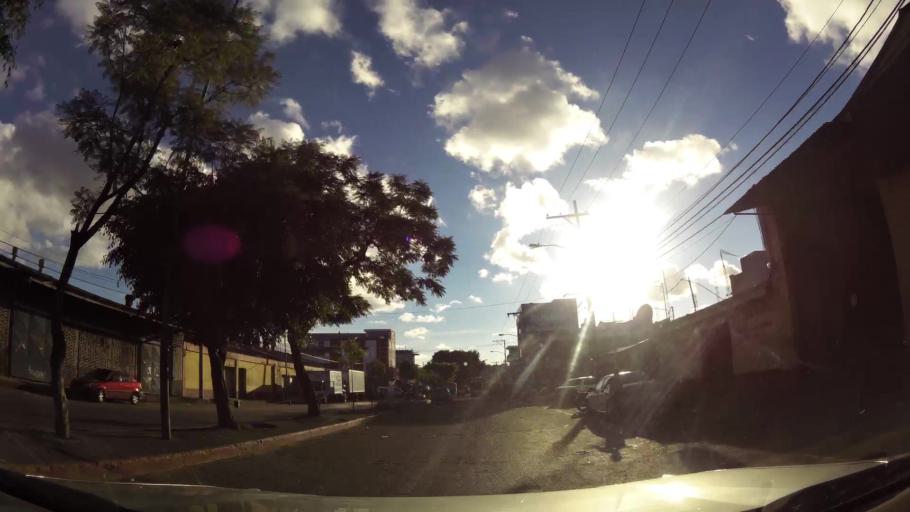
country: GT
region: Guatemala
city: Guatemala City
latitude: 14.6216
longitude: -90.5221
